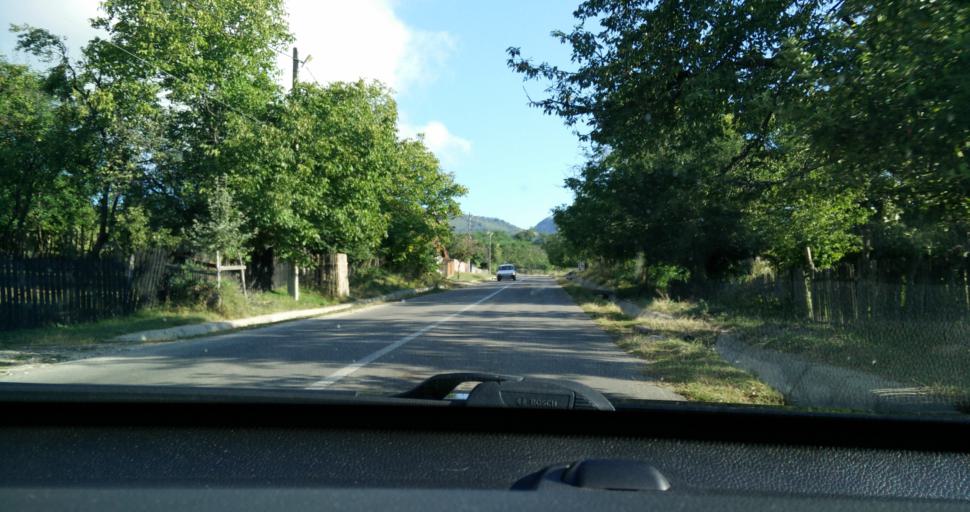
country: RO
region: Gorj
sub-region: Comuna Baia de Fier
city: Baia de Fier
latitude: 45.1750
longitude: 23.7813
